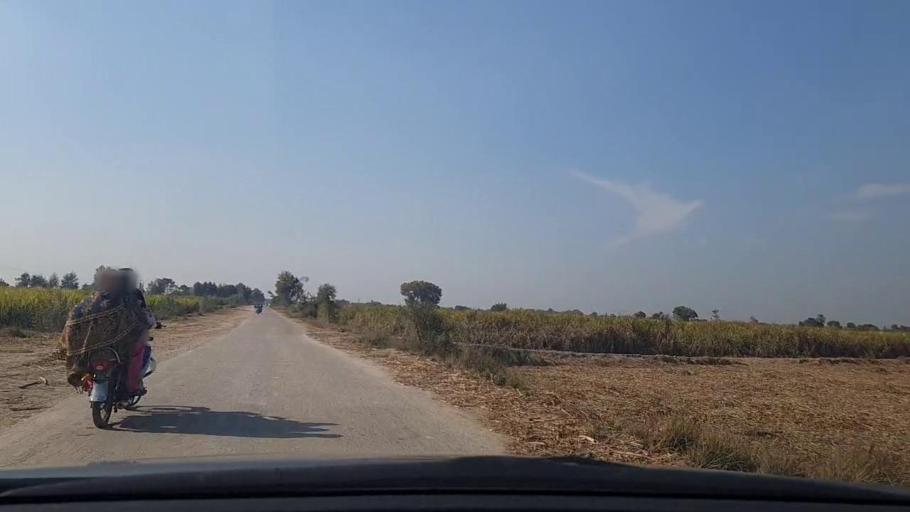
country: PK
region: Sindh
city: Daulatpur
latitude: 26.3101
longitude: 68.0782
